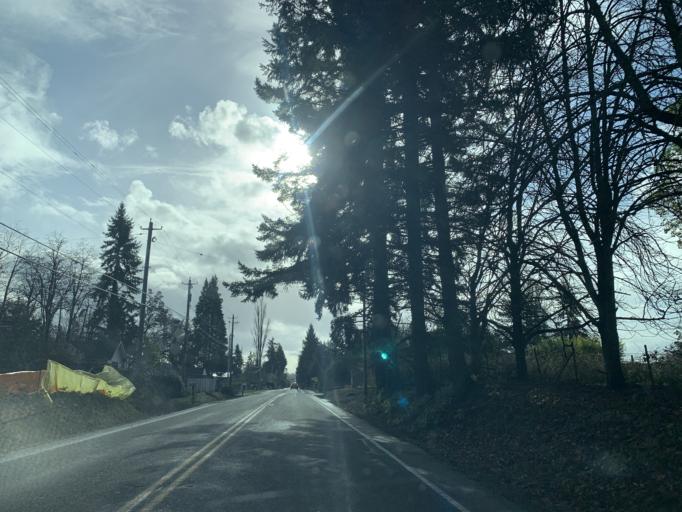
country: US
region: Washington
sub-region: King County
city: Lakeland South
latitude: 47.2747
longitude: -122.2978
